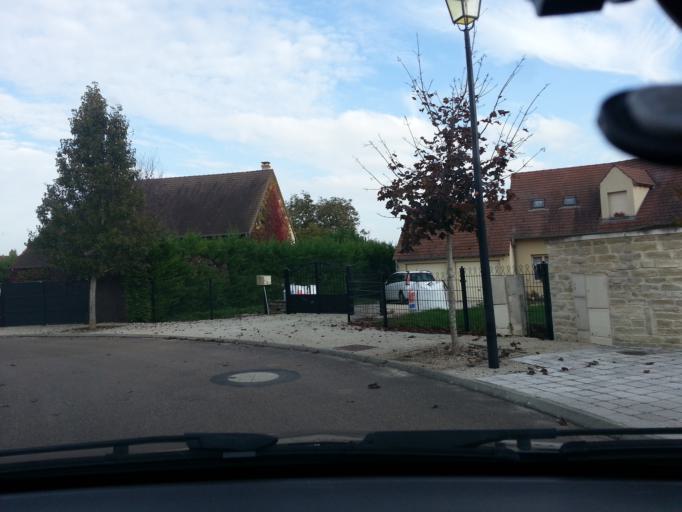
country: FR
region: Bourgogne
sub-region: Departement de Saone-et-Loire
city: Dracy-le-Fort
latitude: 46.7947
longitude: 4.7618
